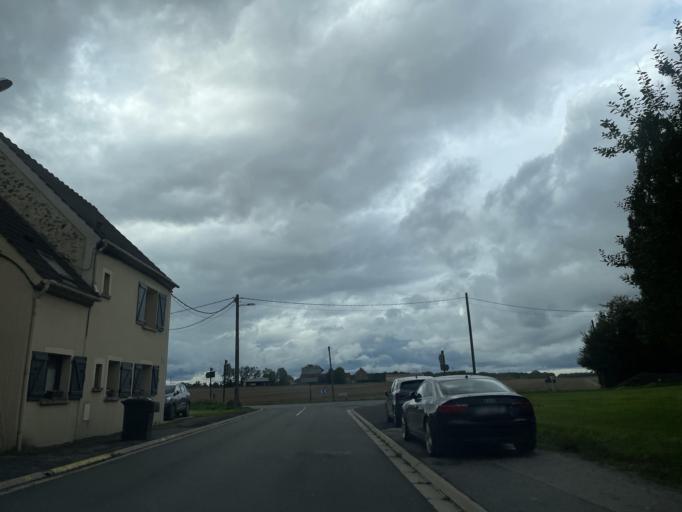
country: FR
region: Ile-de-France
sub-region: Departement de Seine-et-Marne
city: Saint-Jean-les-Deux-Jumeaux
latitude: 48.8999
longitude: 3.0363
